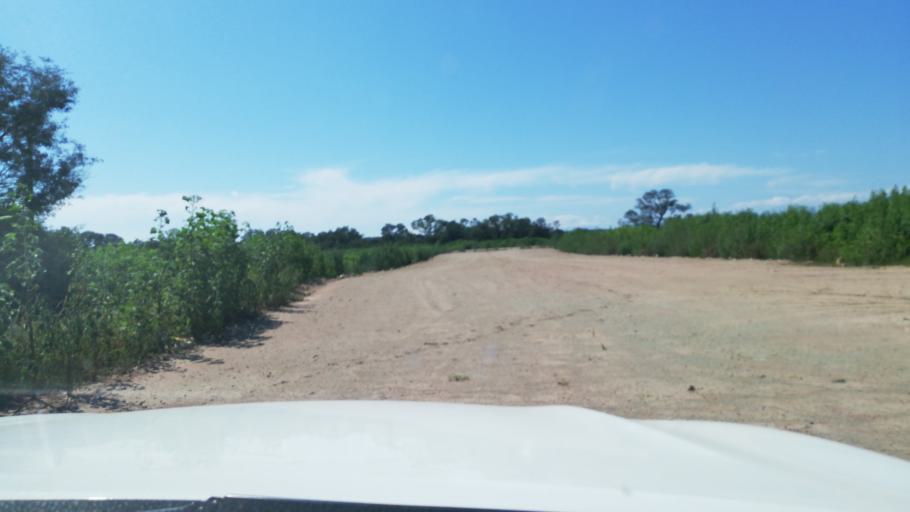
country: AR
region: Jujuy
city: La Mendieta
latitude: -24.3749
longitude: -65.0048
